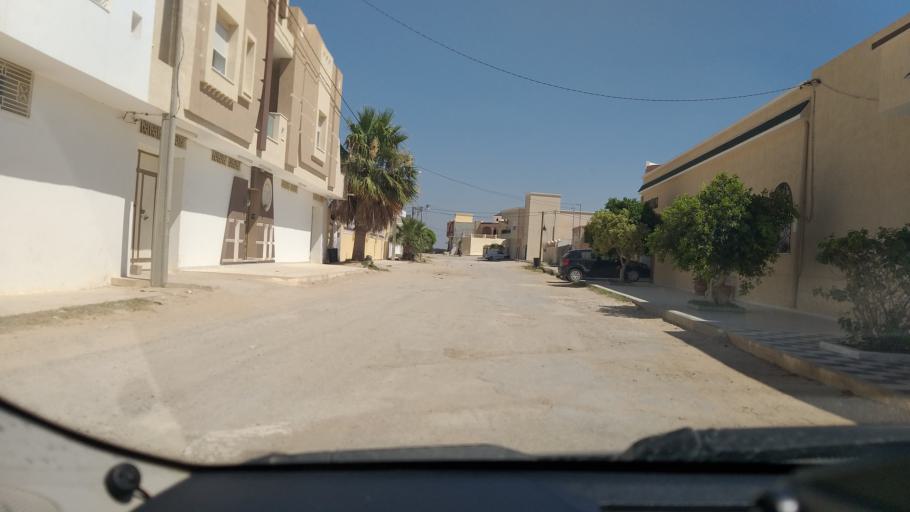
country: TN
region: Al Mahdiyah
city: El Jem
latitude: 35.2892
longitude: 10.7177
